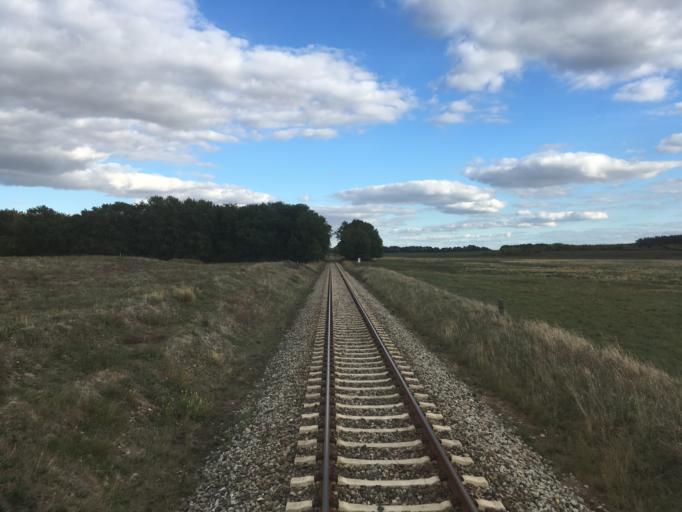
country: DE
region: Mecklenburg-Vorpommern
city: Grabowhofe
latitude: 53.5420
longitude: 12.5863
